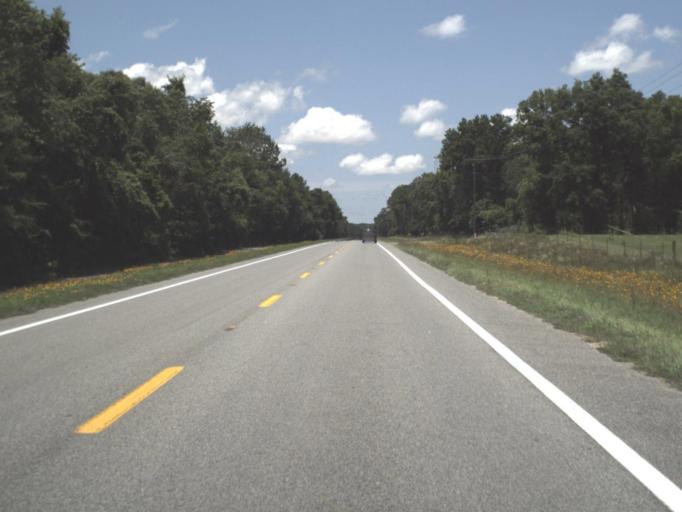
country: US
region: Florida
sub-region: Alachua County
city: High Springs
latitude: 29.9504
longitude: -82.7667
